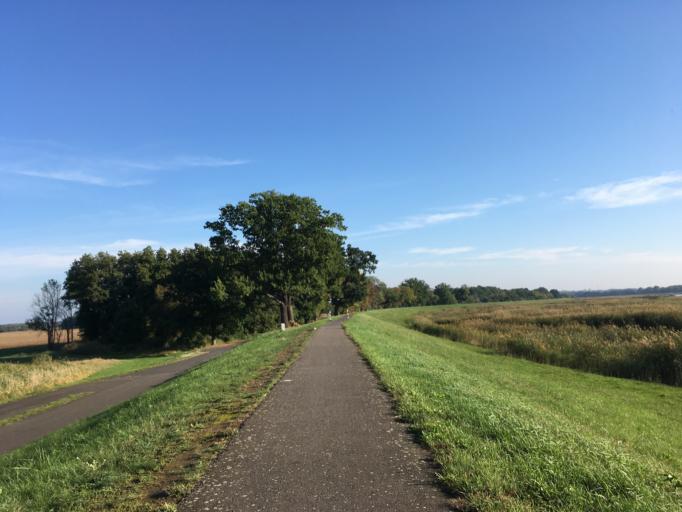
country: DE
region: Brandenburg
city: Reitwein
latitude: 52.4761
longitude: 14.6086
